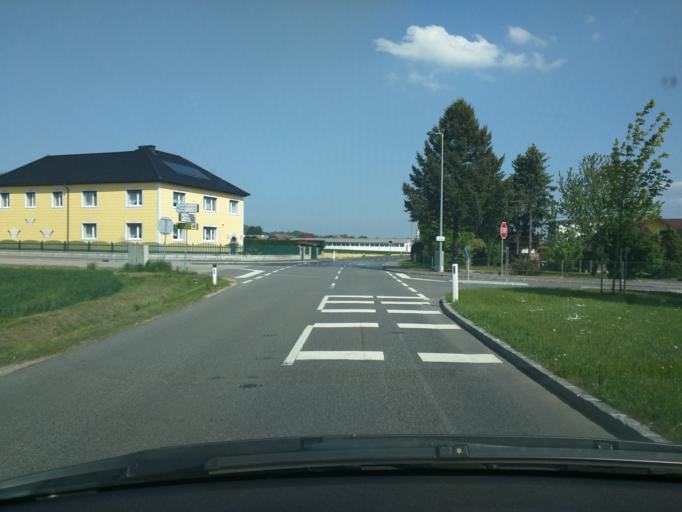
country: AT
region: Lower Austria
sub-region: Politischer Bezirk Melk
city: Blindenmarkt
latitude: 48.1295
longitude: 14.9787
